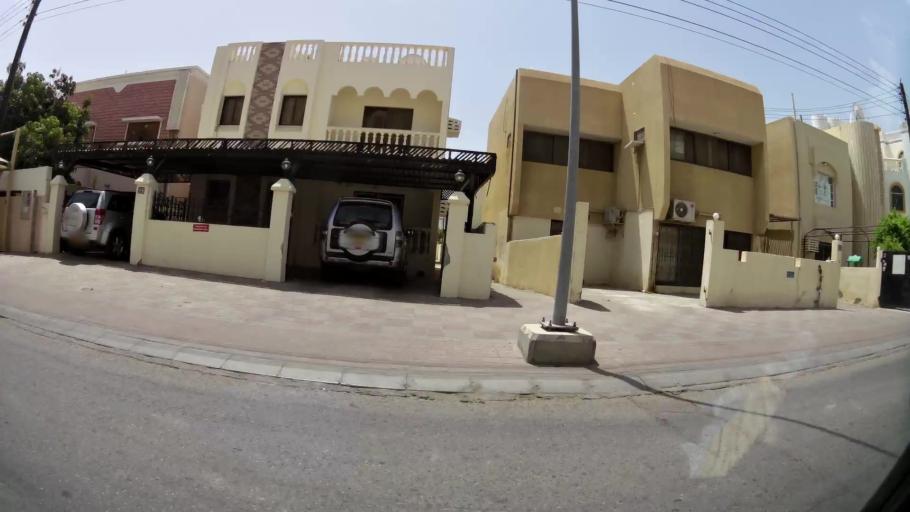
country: OM
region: Muhafazat Masqat
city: Bawshar
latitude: 23.5933
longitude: 58.4342
